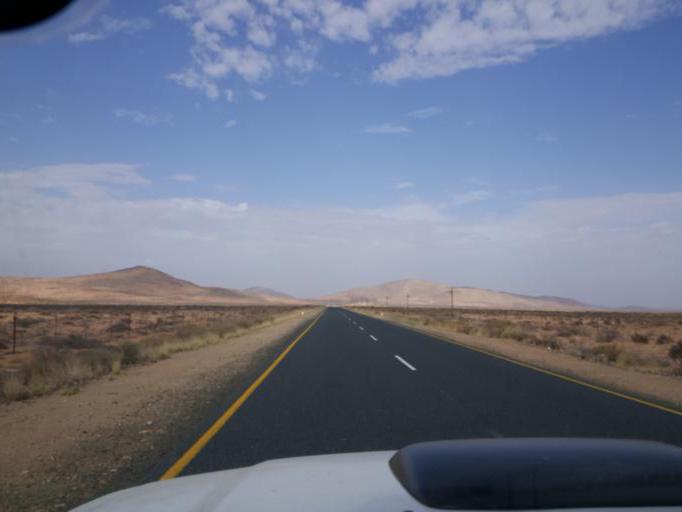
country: ZA
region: Northern Cape
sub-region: Namakwa District Municipality
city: Springbok
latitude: -29.2534
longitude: 17.5489
